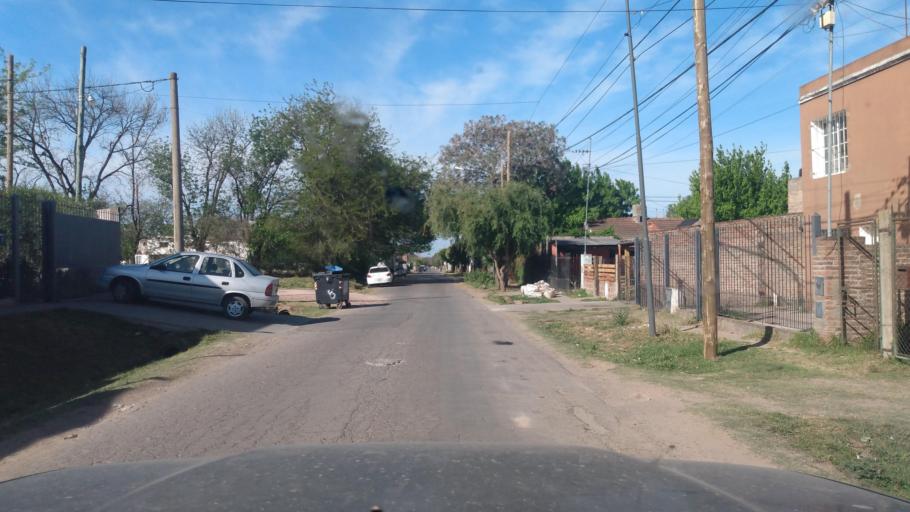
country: AR
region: Buenos Aires
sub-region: Partido de Lujan
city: Lujan
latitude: -34.5672
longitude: -59.1362
